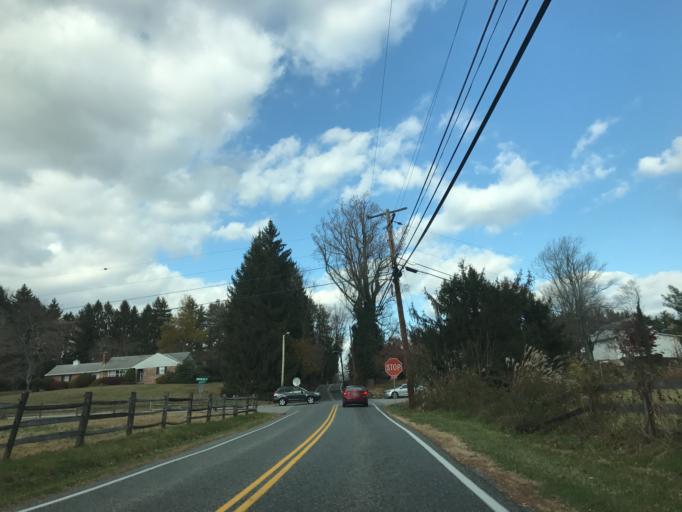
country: US
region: Maryland
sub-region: Harford County
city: Pleasant Hills
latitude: 39.5014
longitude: -76.3736
